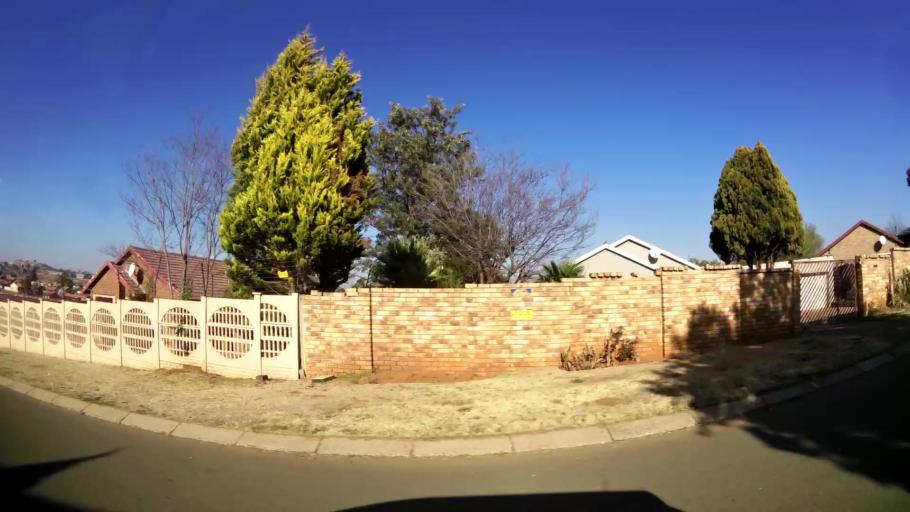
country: ZA
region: Gauteng
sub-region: City of Johannesburg Metropolitan Municipality
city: Roodepoort
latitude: -26.1531
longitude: 27.8438
